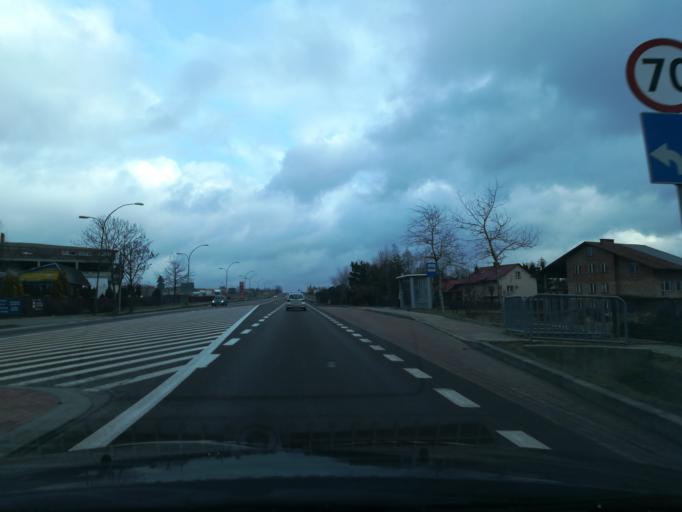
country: PL
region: Subcarpathian Voivodeship
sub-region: Powiat lancucki
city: Kraczkowa
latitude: 50.0460
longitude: 22.1504
